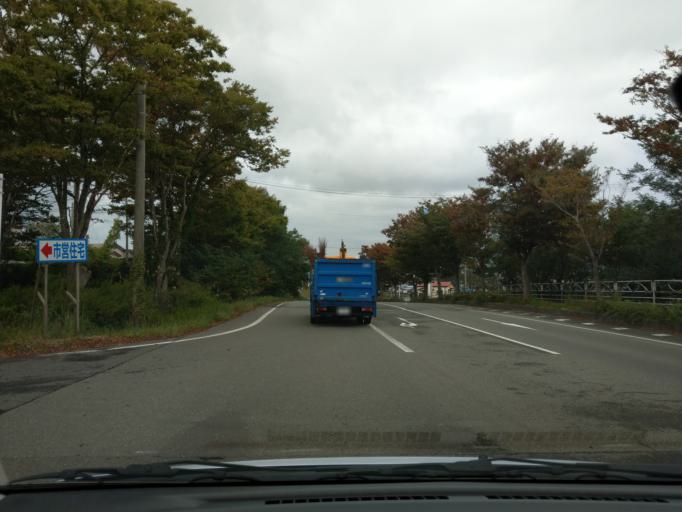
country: JP
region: Akita
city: Akita Shi
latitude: 39.6761
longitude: 140.0786
